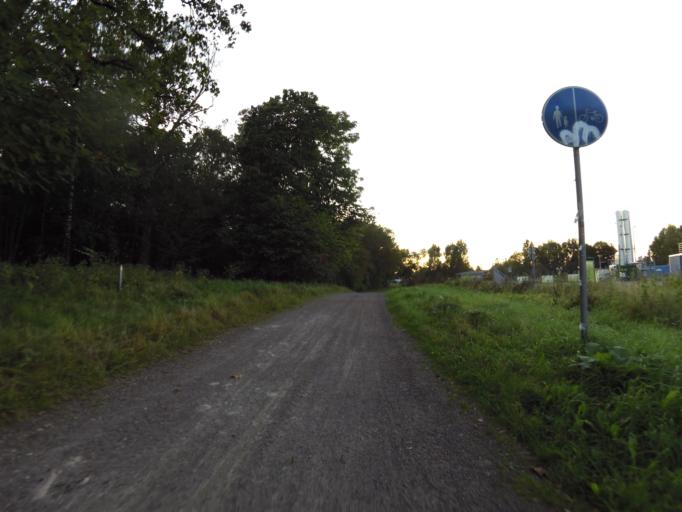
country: SE
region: Gaevleborg
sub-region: Gavle Kommun
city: Gavle
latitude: 60.6734
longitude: 17.1876
